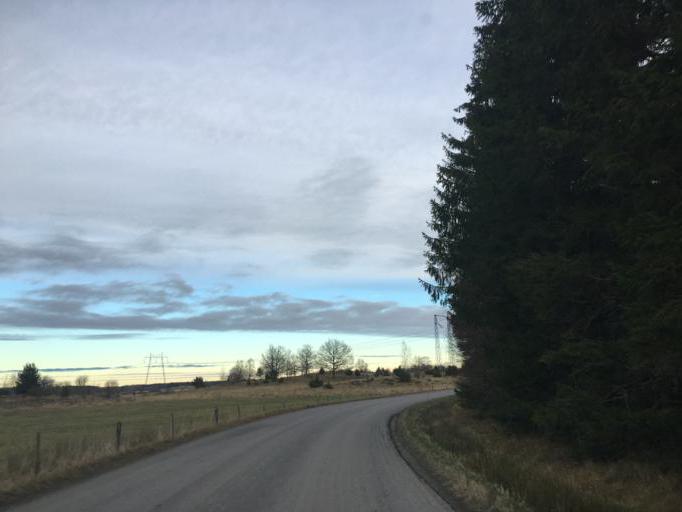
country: SE
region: OEstergoetland
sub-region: Norrkopings Kommun
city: Kimstad
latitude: 58.4322
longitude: 16.0710
